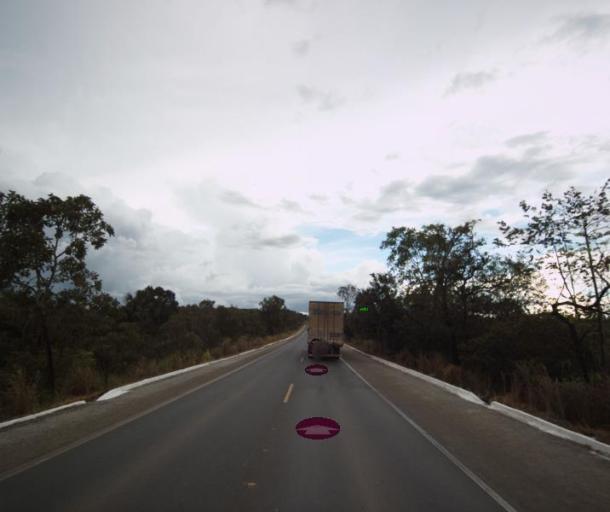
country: BR
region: Goias
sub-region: Itapaci
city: Itapaci
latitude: -14.9395
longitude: -49.3708
